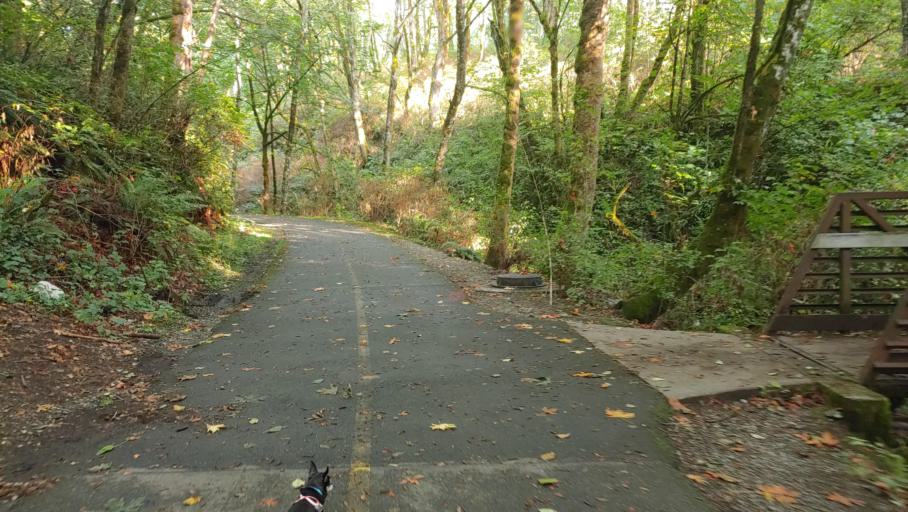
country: US
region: Washington
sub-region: King County
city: Des Moines
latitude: 47.4132
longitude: -122.3113
